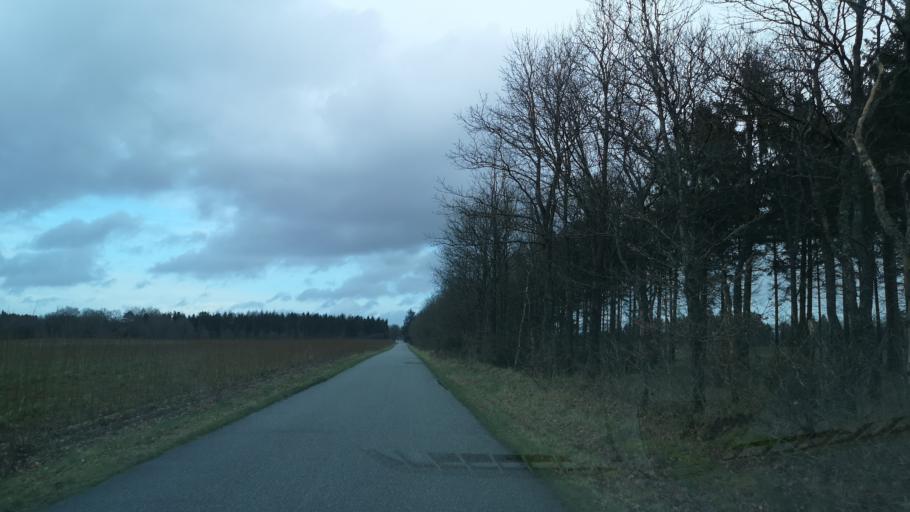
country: DK
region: Central Jutland
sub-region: Herning Kommune
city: Lind
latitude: 55.9973
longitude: 8.9662
